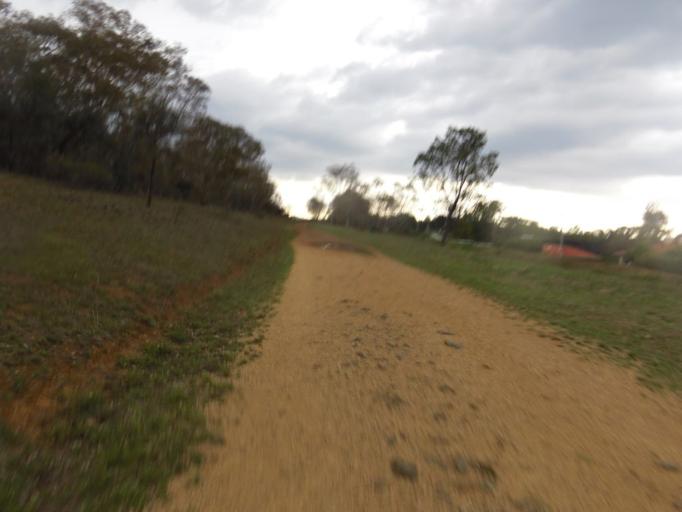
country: AU
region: Australian Capital Territory
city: Forrest
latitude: -35.3240
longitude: 149.1184
